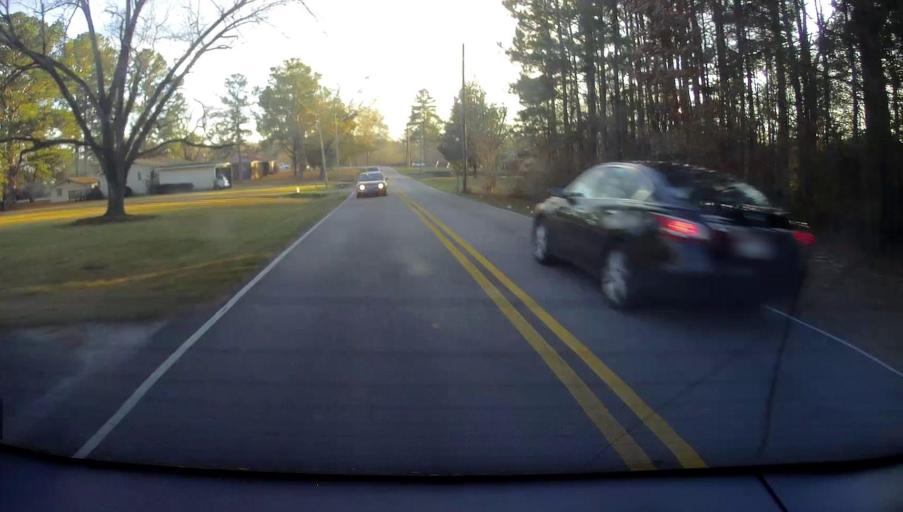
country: US
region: Alabama
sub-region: Etowah County
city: Gadsden
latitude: 33.9803
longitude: -85.9846
